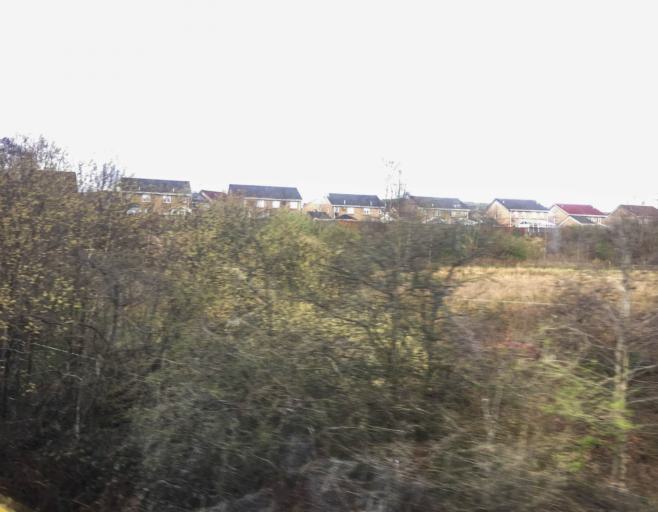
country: GB
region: Scotland
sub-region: West Dunbartonshire
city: Old Kilpatrick
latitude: 55.9197
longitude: -4.4447
